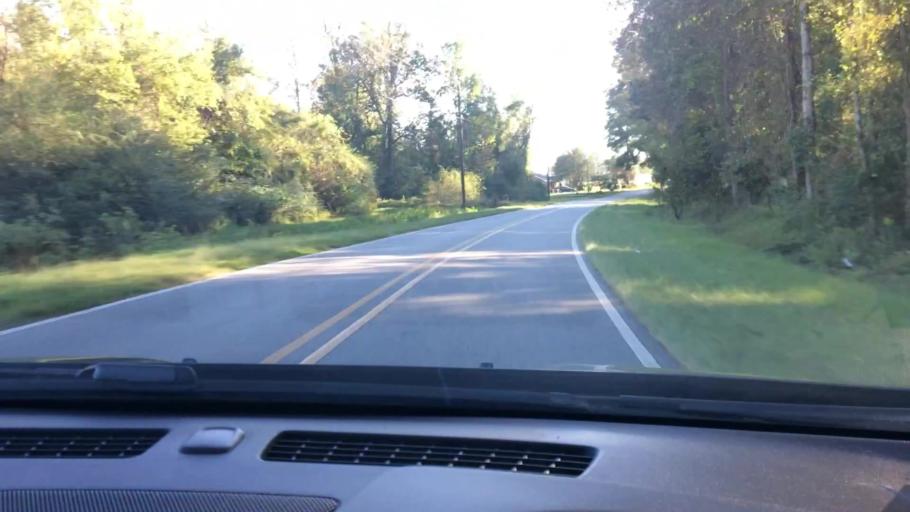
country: US
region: North Carolina
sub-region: Pitt County
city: Winterville
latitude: 35.5150
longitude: -77.4313
